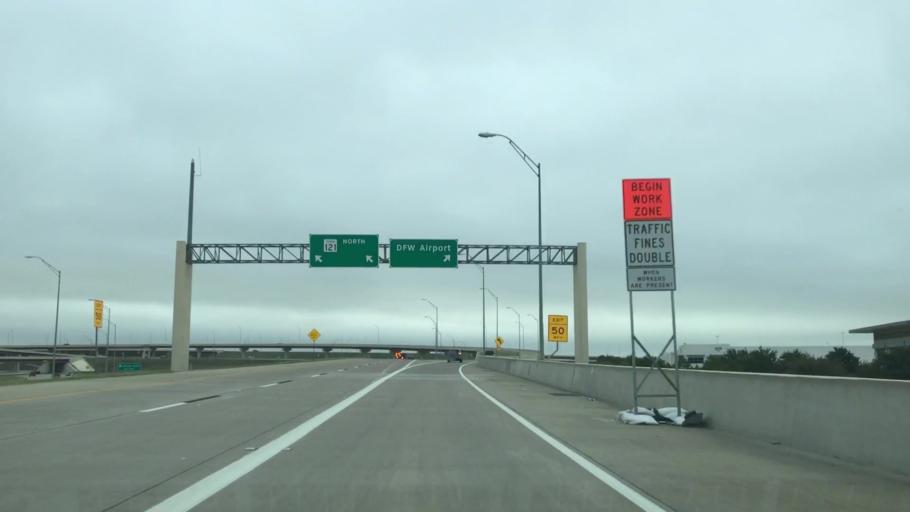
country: US
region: Texas
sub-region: Dallas County
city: Coppell
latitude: 32.9318
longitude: -97.0342
